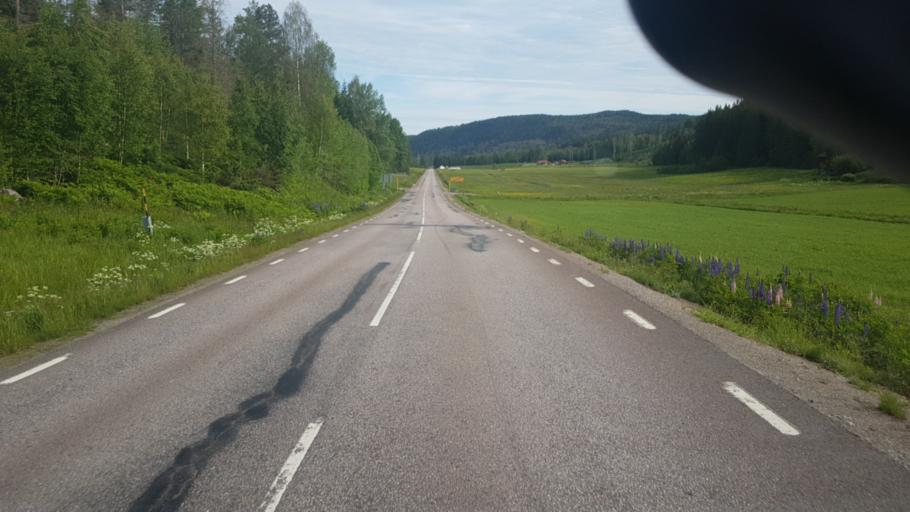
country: SE
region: Vaermland
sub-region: Arvika Kommun
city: Arvika
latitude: 59.7312
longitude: 12.6432
